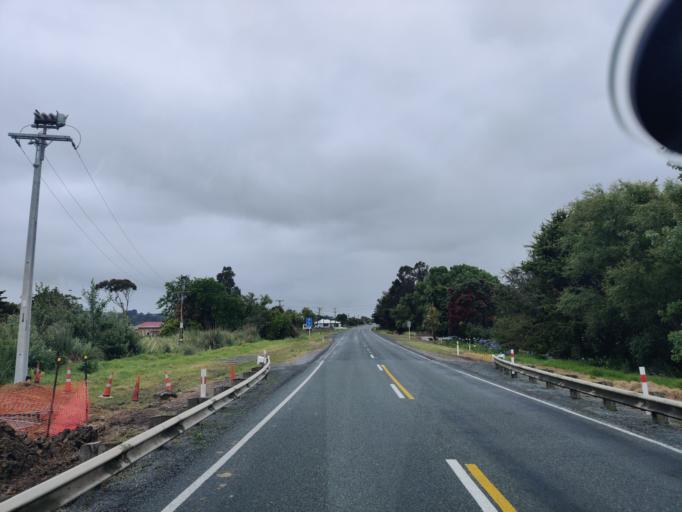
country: NZ
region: Northland
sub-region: Kaipara District
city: Dargaville
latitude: -35.9414
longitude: 173.8856
